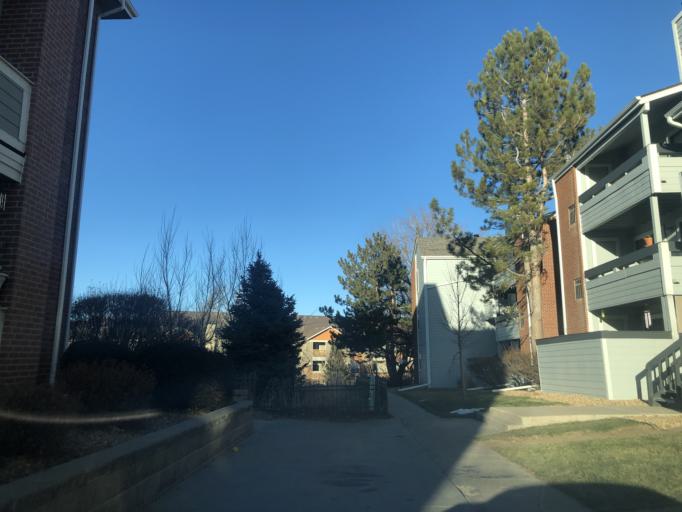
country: US
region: Colorado
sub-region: Adams County
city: Aurora
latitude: 39.7188
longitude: -104.8210
